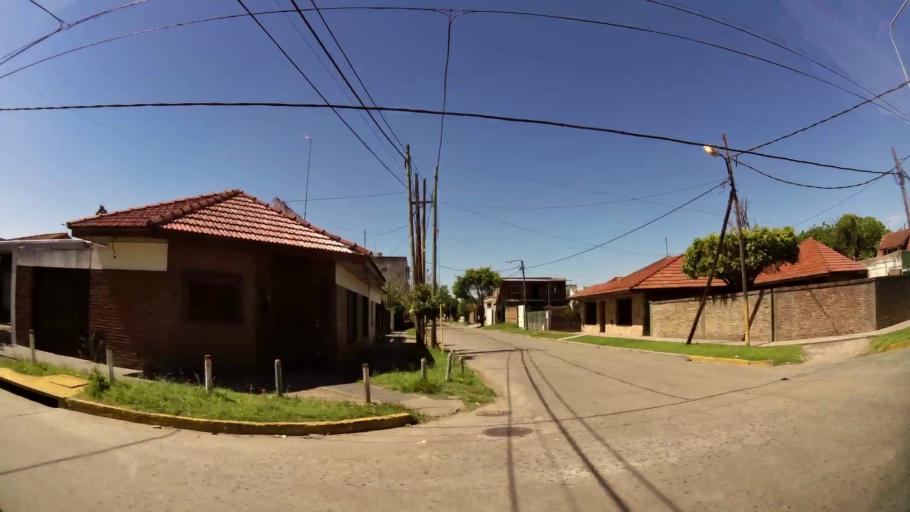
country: AR
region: Buenos Aires
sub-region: Partido de Quilmes
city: Quilmes
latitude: -34.7294
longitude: -58.3006
